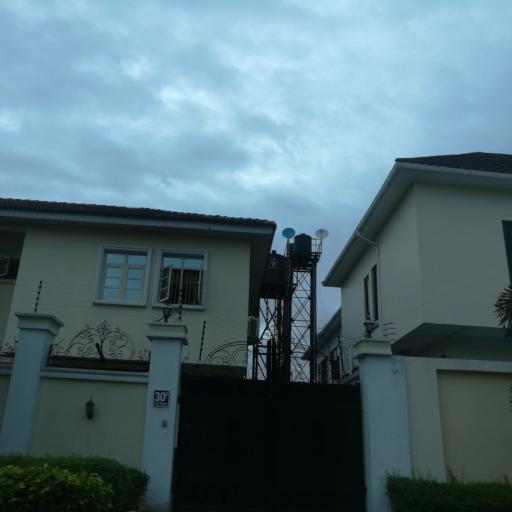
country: NG
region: Lagos
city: Ikoyi
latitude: 6.4414
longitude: 3.4721
